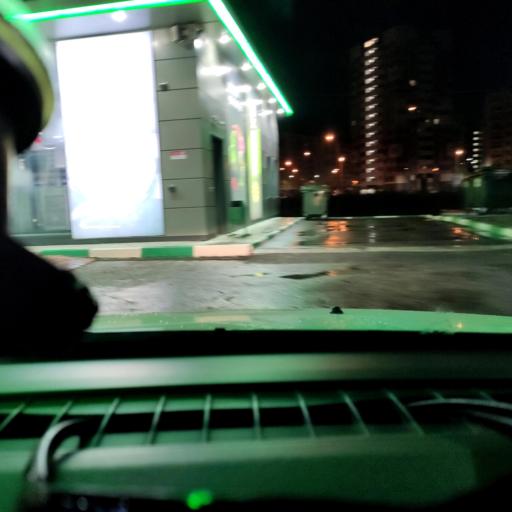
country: RU
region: Samara
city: Samara
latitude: 53.0958
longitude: 50.1578
